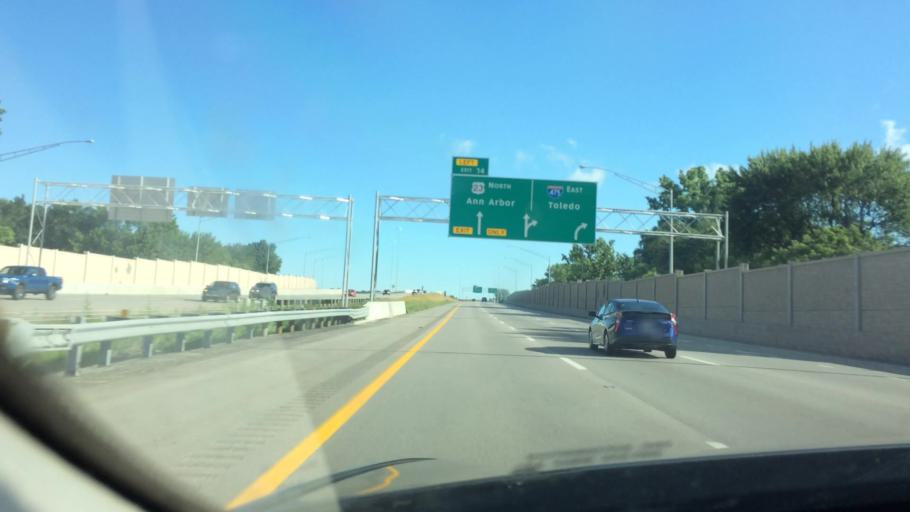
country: US
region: Ohio
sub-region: Lucas County
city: Sylvania
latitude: 41.6791
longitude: -83.6942
